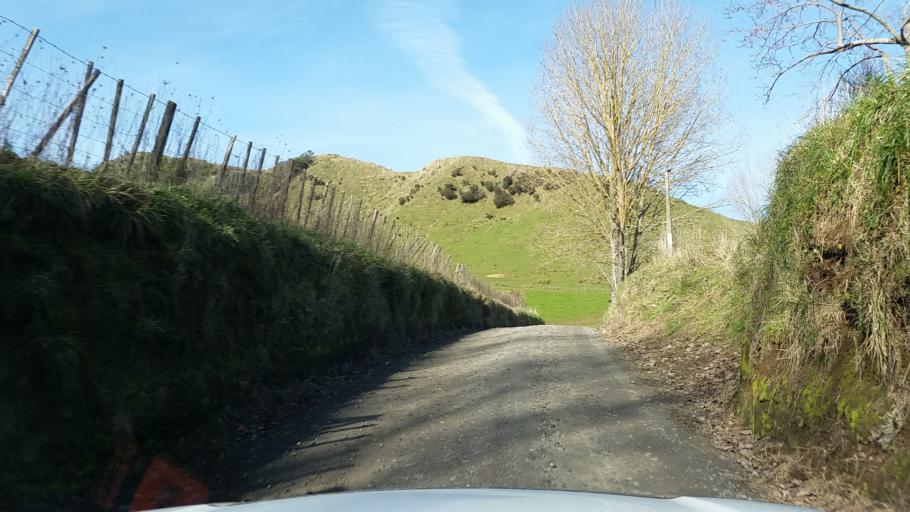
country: NZ
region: Taranaki
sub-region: South Taranaki District
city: Eltham
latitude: -39.3540
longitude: 174.5137
